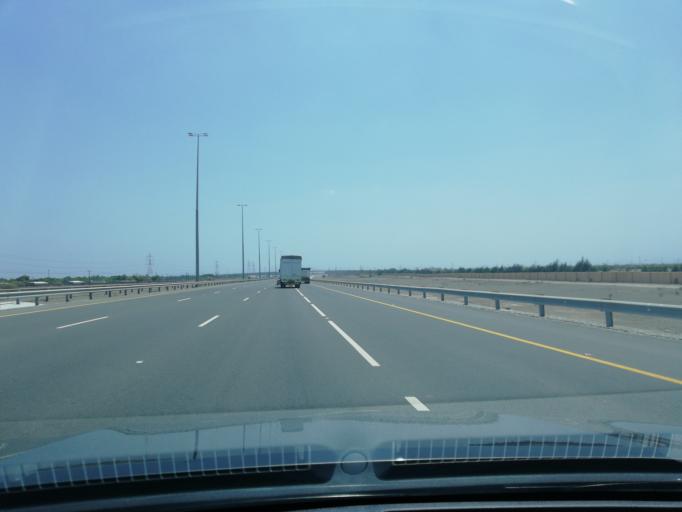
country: OM
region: Al Batinah
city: Barka'
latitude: 23.6311
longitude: 57.9754
